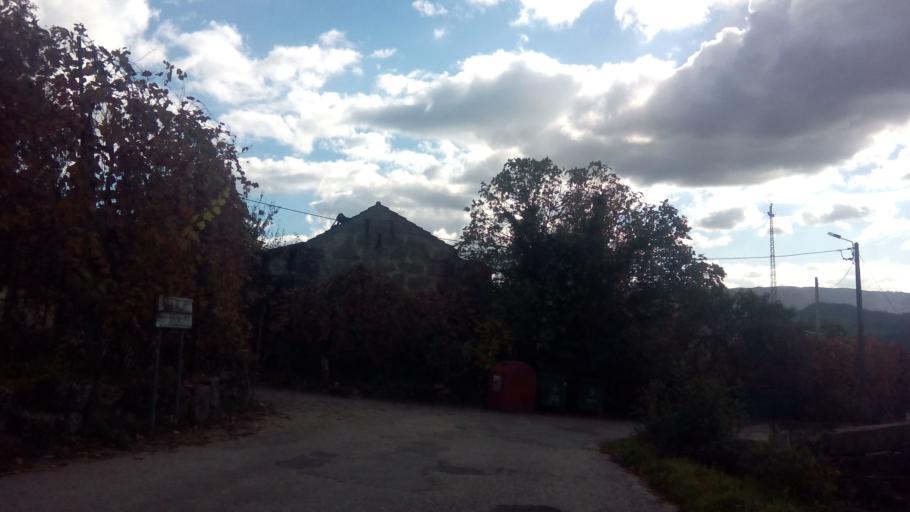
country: PT
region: Porto
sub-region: Amarante
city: Amarante
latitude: 41.2831
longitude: -7.9918
